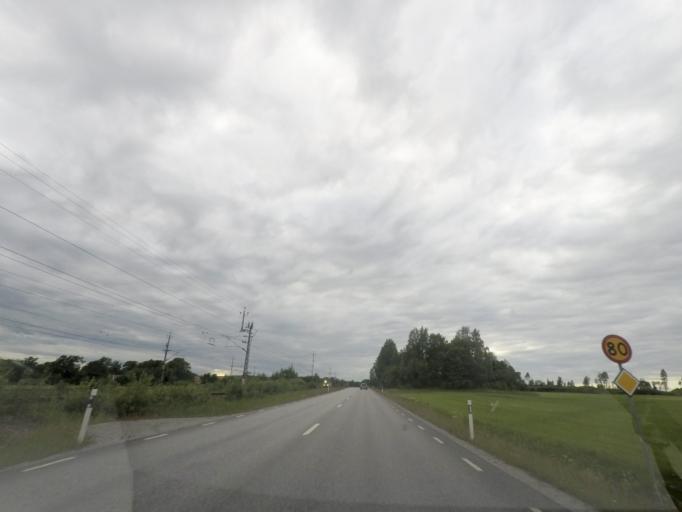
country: SE
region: Vaestmanland
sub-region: Arboga Kommun
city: Arboga
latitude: 59.4087
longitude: 15.7952
